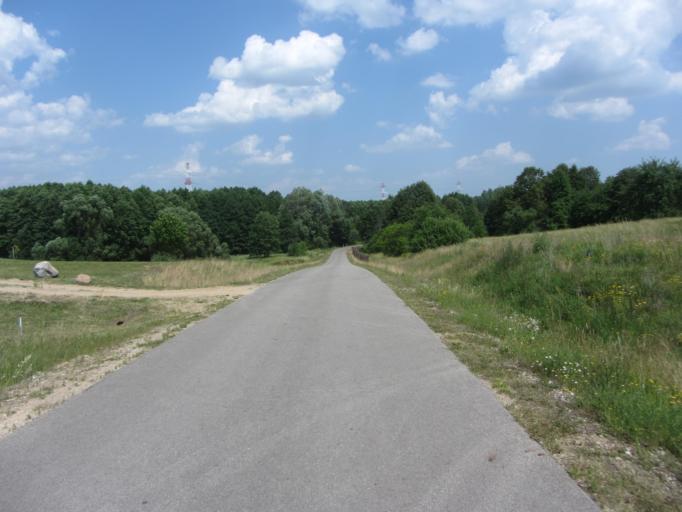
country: PL
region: Podlasie
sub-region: Powiat sejnenski
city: Sejny
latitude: 54.2241
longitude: 23.3922
